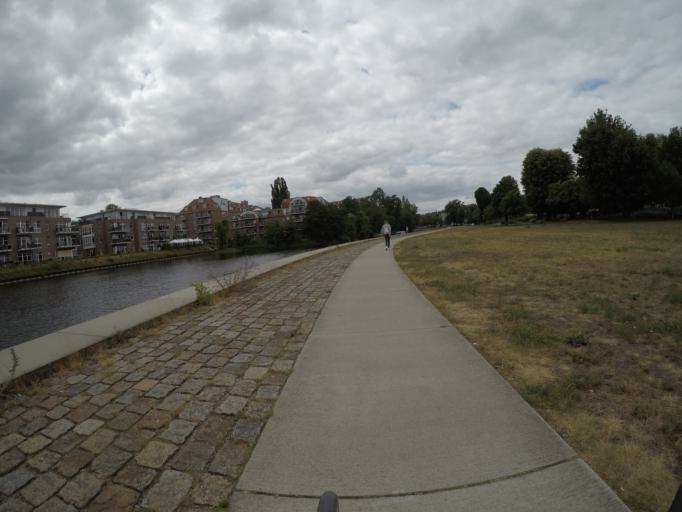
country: DE
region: Berlin
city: Hakenfelde
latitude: 52.5548
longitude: 13.2118
